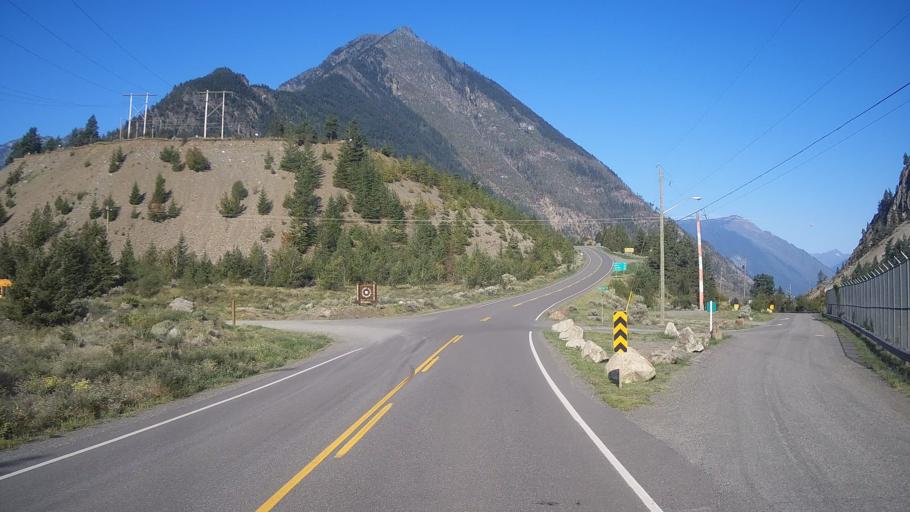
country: CA
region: British Columbia
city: Lillooet
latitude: 50.6688
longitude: -121.9777
